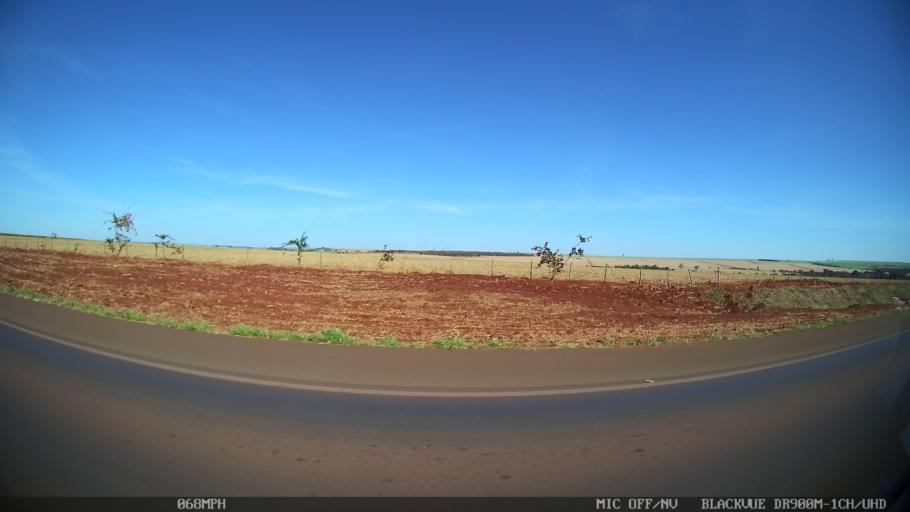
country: BR
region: Sao Paulo
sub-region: Ipua
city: Ipua
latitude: -20.4949
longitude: -47.9773
